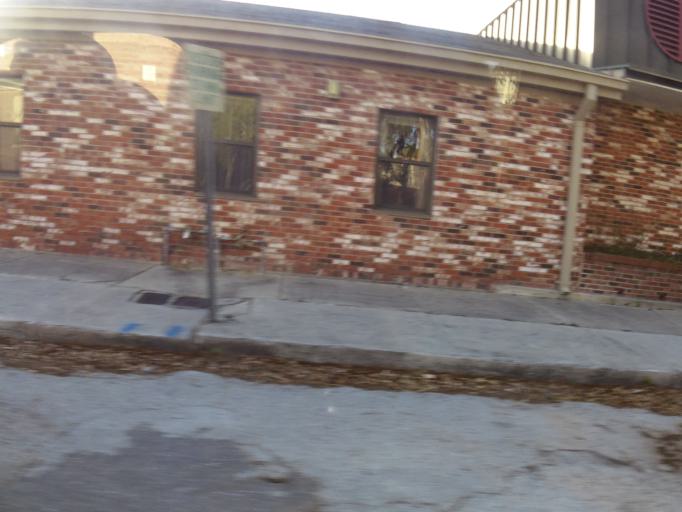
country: US
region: Florida
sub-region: Clay County
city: Green Cove Springs
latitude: 29.9923
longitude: -81.6840
